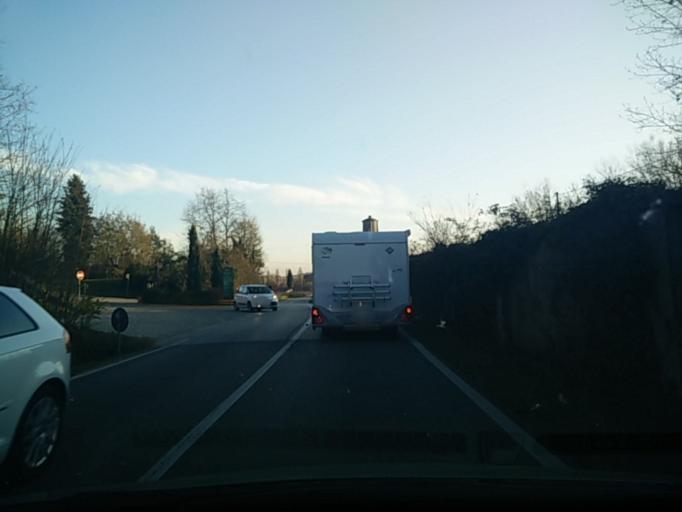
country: IT
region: Lombardy
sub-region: Provincia di Mantova
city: Ponti sul Mincio
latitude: 45.4236
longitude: 10.7058
